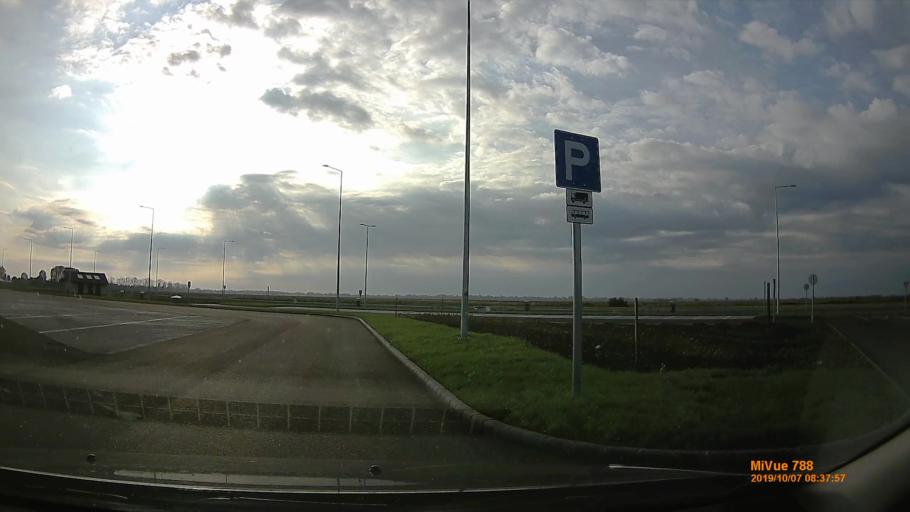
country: HU
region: Bekes
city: Bekesszentandras
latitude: 46.8268
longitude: 20.4734
